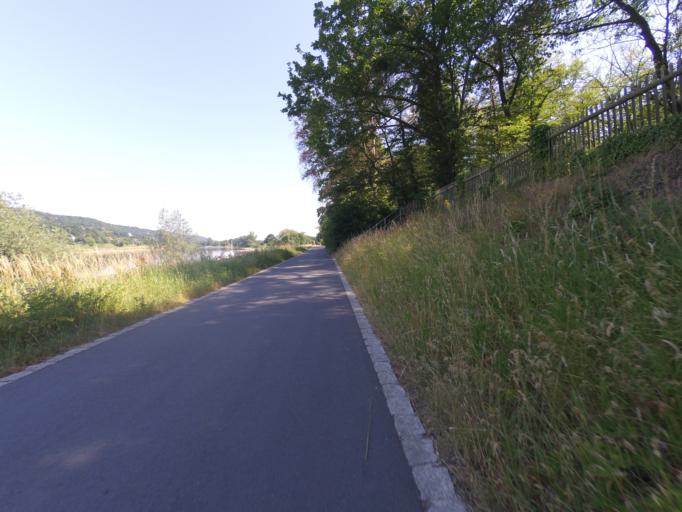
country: DE
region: Saxony
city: Albertstadt
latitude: 51.0417
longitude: 13.8177
